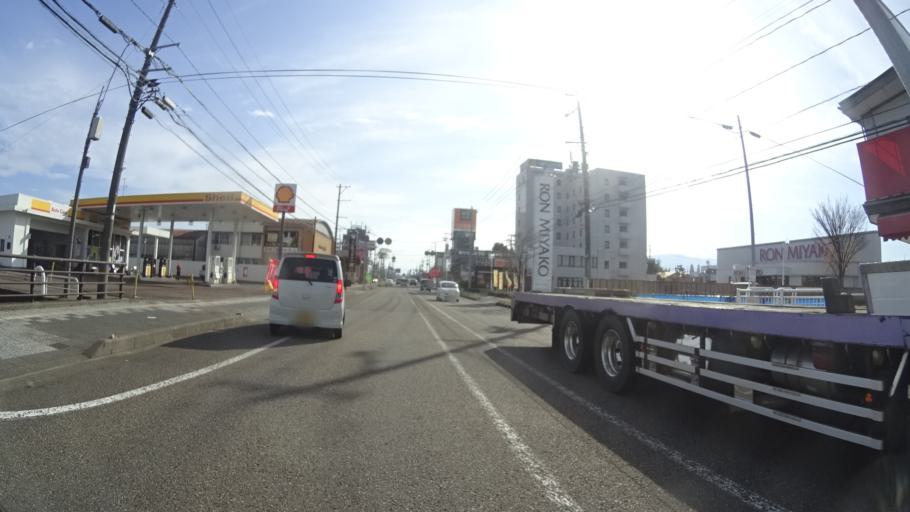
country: JP
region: Niigata
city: Joetsu
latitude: 37.1527
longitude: 138.2385
